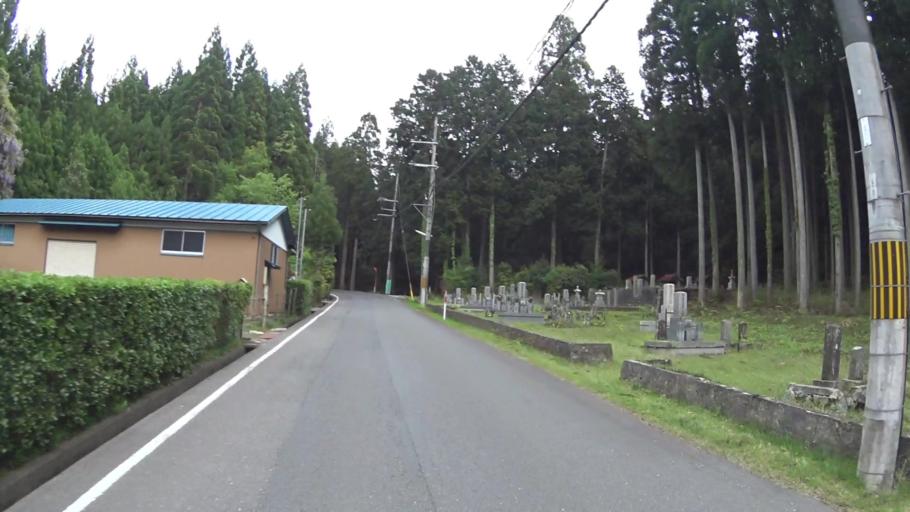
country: JP
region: Kyoto
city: Kameoka
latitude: 35.1896
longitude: 135.6379
